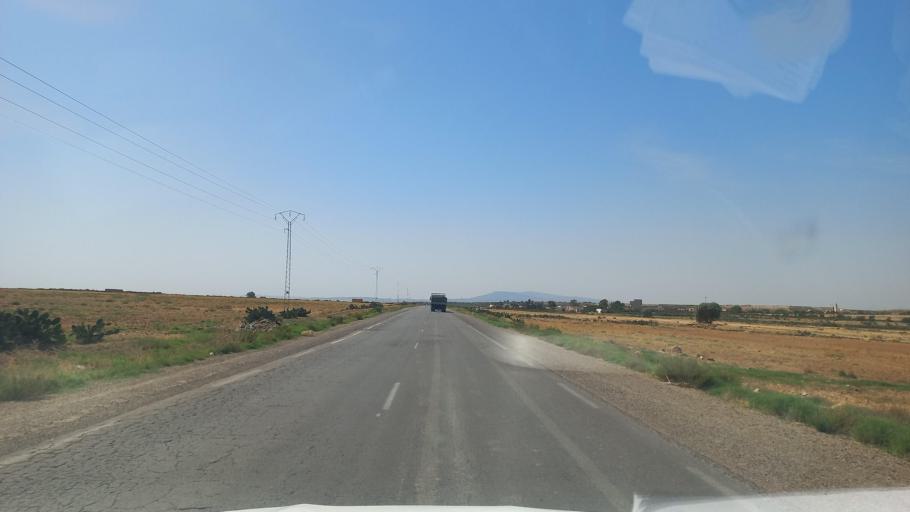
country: TN
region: Al Qasrayn
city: Sbiba
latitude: 35.3687
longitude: 9.0969
